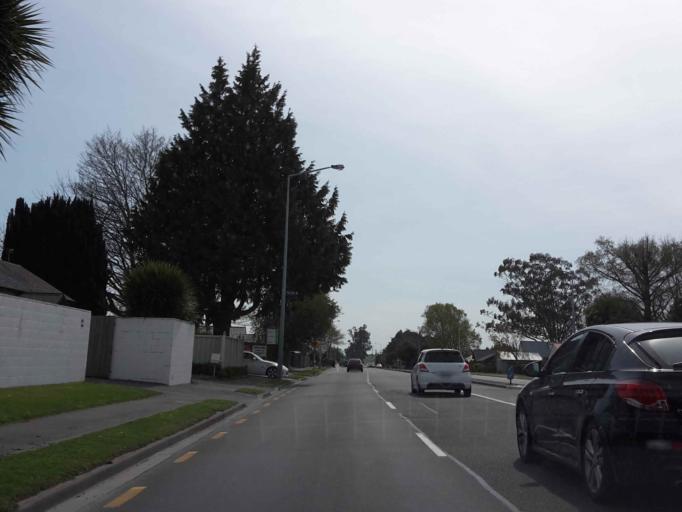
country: NZ
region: Canterbury
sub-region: Waimakariri District
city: Kaiapoi
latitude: -43.4435
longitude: 172.6334
